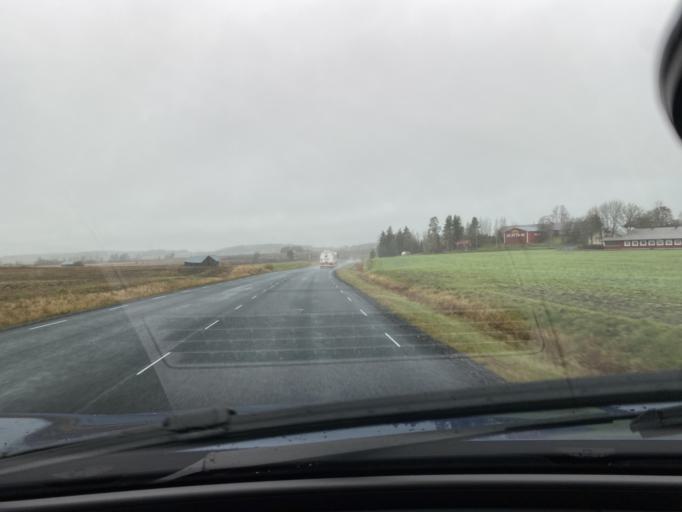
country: FI
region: Haeme
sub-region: Forssa
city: Ypaejae
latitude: 60.7800
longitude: 23.3093
